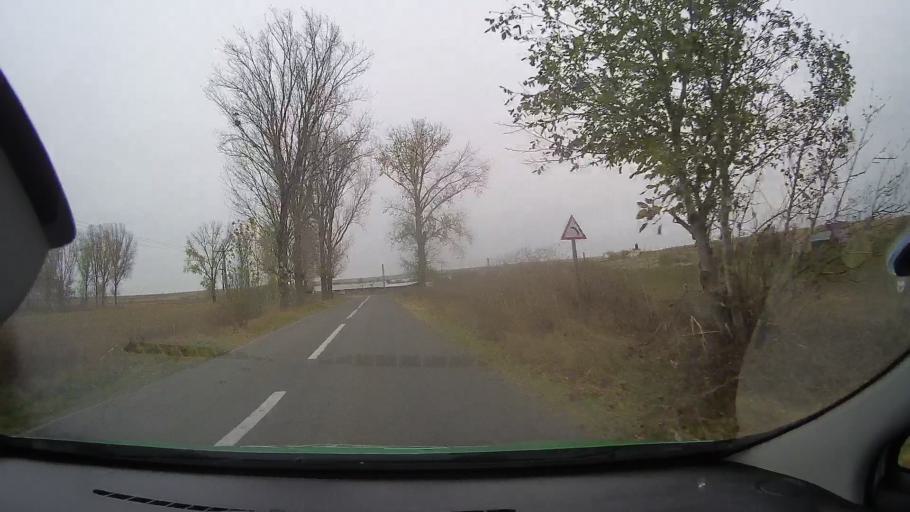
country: RO
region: Constanta
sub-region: Comuna Saraiu
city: Saraiu
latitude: 44.7254
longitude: 28.2206
